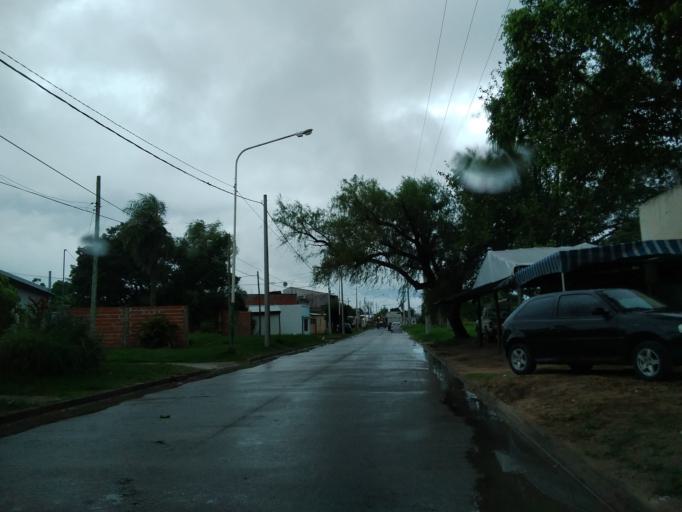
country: AR
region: Corrientes
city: Corrientes
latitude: -27.4961
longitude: -58.8231
